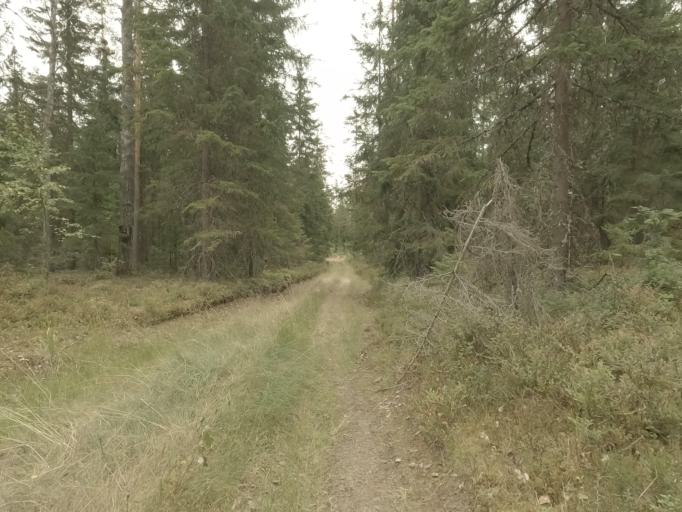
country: RU
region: Leningrad
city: Kamennogorsk
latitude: 61.0521
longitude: 29.1781
